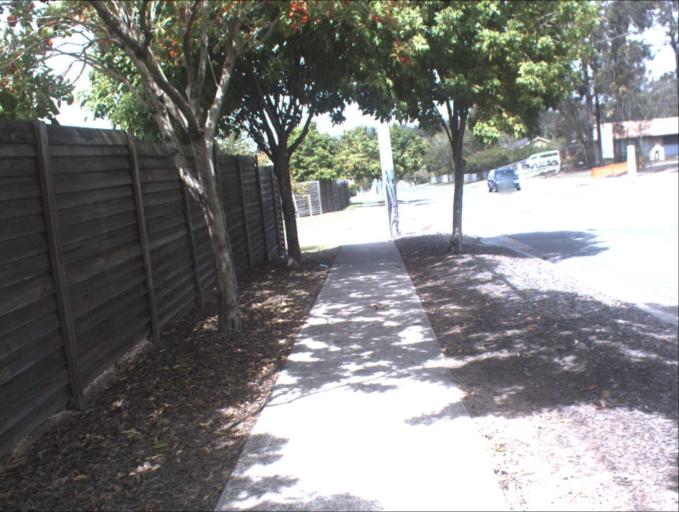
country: AU
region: Queensland
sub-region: Logan
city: Park Ridge South
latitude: -27.6880
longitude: 153.0228
